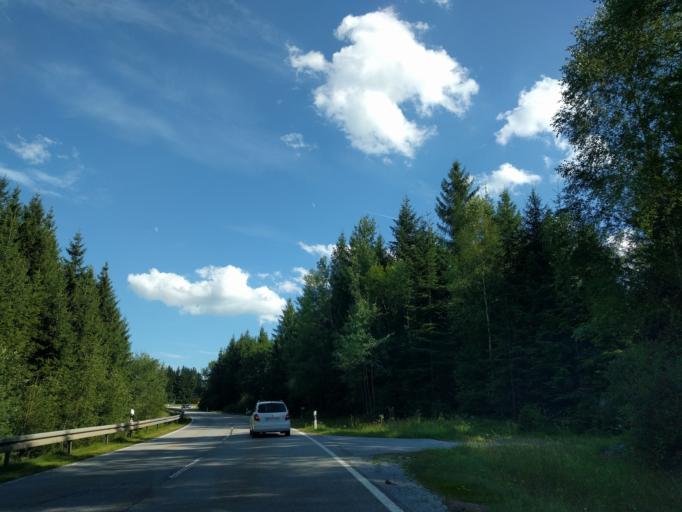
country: DE
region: Bavaria
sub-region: Lower Bavaria
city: Langdorf
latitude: 49.0194
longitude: 13.1389
